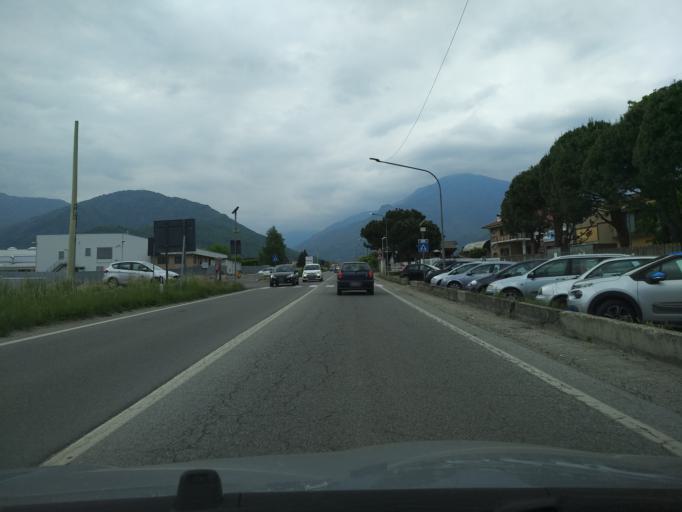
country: IT
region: Piedmont
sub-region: Provincia di Torino
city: Airali
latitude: 44.8119
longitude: 7.2641
